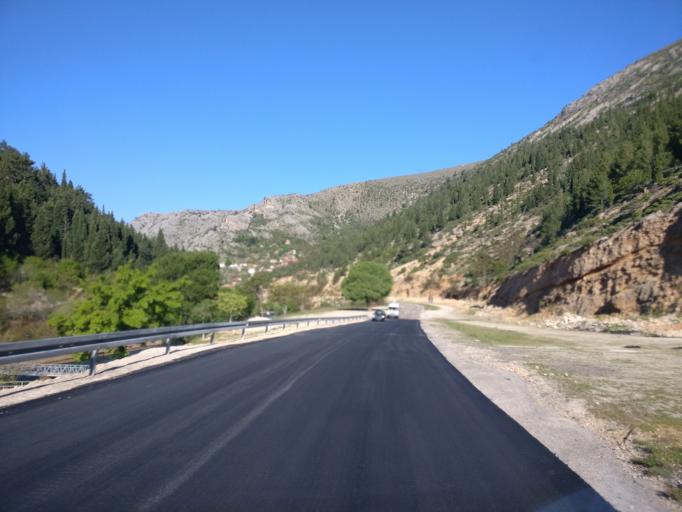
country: BA
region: Federation of Bosnia and Herzegovina
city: Stolac
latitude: 43.0987
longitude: 17.9851
